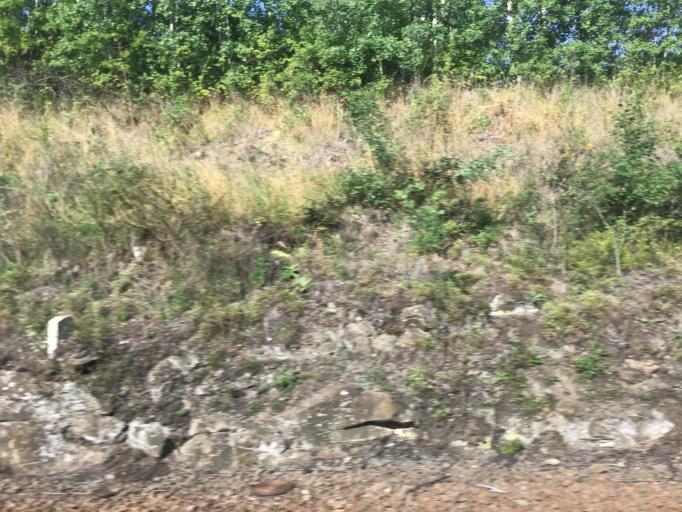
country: CZ
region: Jihocesky
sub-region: Okres Tabor
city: Tabor
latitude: 49.4254
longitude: 14.6677
